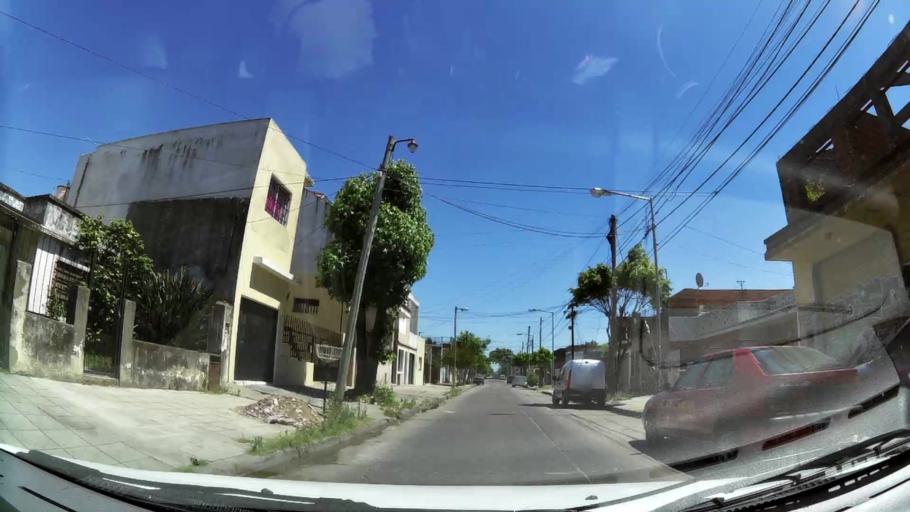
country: AR
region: Buenos Aires
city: Caseros
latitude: -34.5809
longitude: -58.5615
